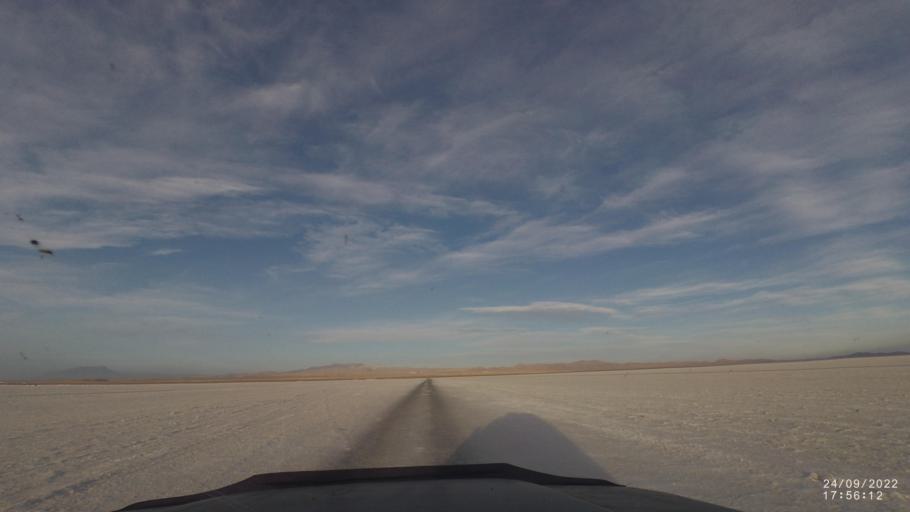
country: BO
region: Potosi
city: Colchani
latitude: -20.3249
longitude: -67.0170
